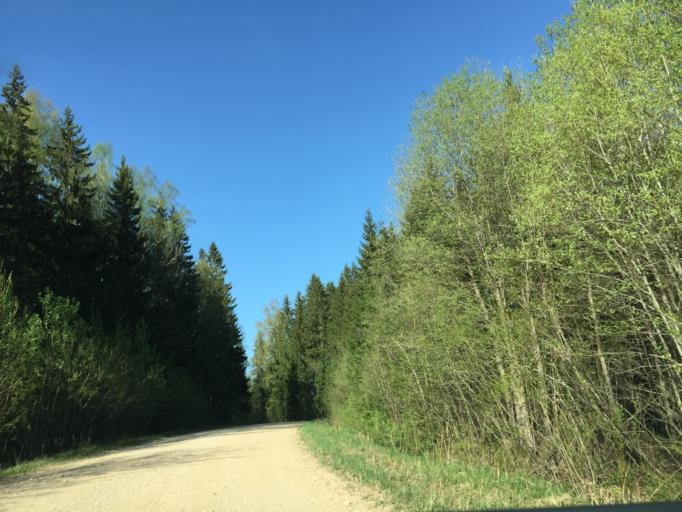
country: LV
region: Ergli
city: Ergli
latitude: 56.9130
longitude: 25.4489
